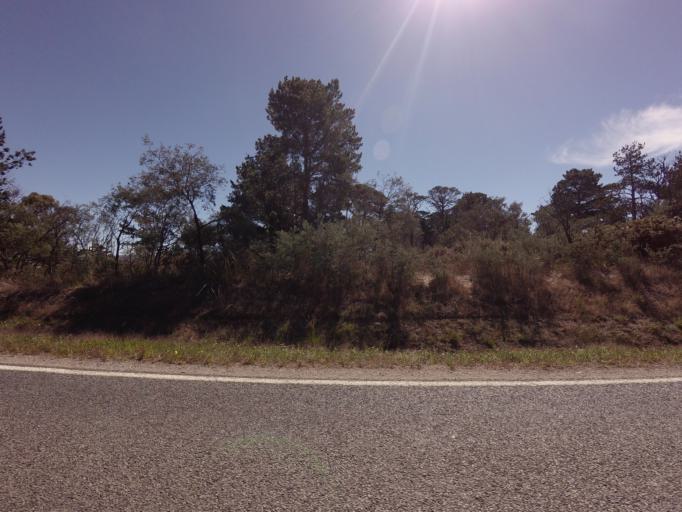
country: AU
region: Tasmania
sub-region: Northern Midlands
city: Evandale
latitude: -41.7864
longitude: 147.7160
